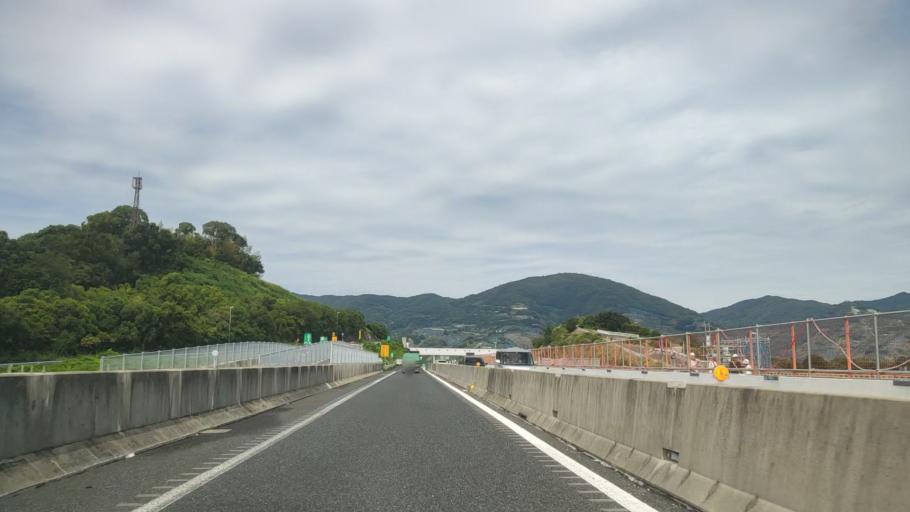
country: JP
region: Wakayama
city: Kainan
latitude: 34.0578
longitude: 135.2007
